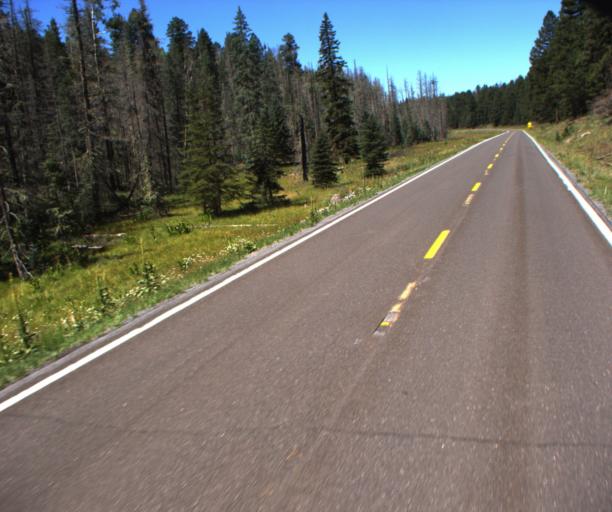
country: US
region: Arizona
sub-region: Apache County
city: Eagar
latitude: 33.6488
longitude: -109.3037
